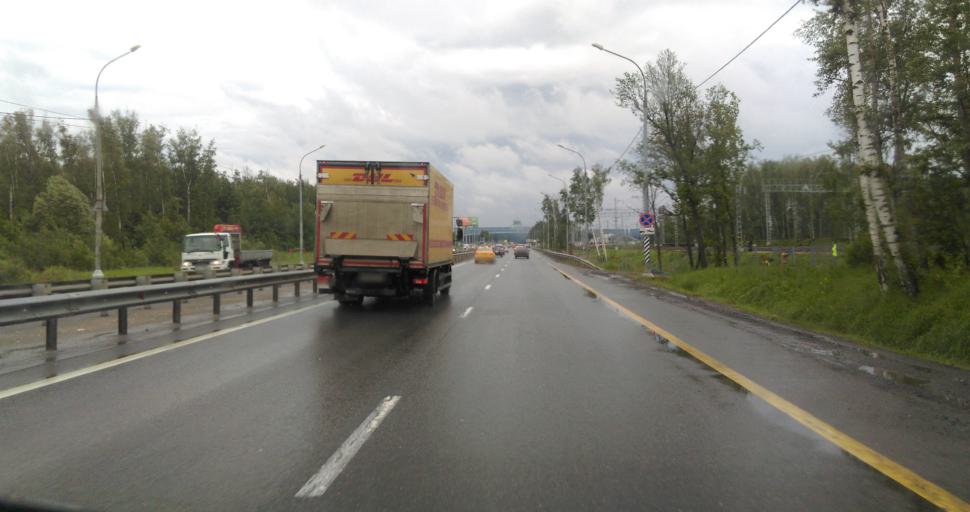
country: RU
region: Moskovskaya
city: Yakovlevskoye
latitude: 55.4235
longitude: 37.8888
